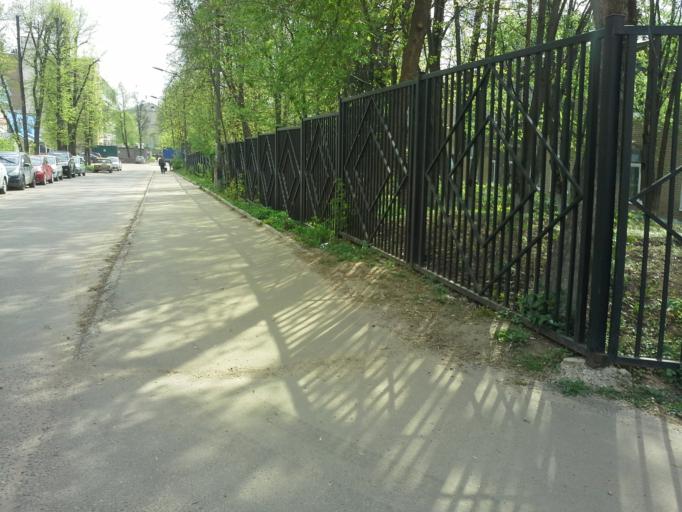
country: RU
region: Moskovskaya
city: Sergiyev Posad
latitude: 56.3208
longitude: 38.1457
